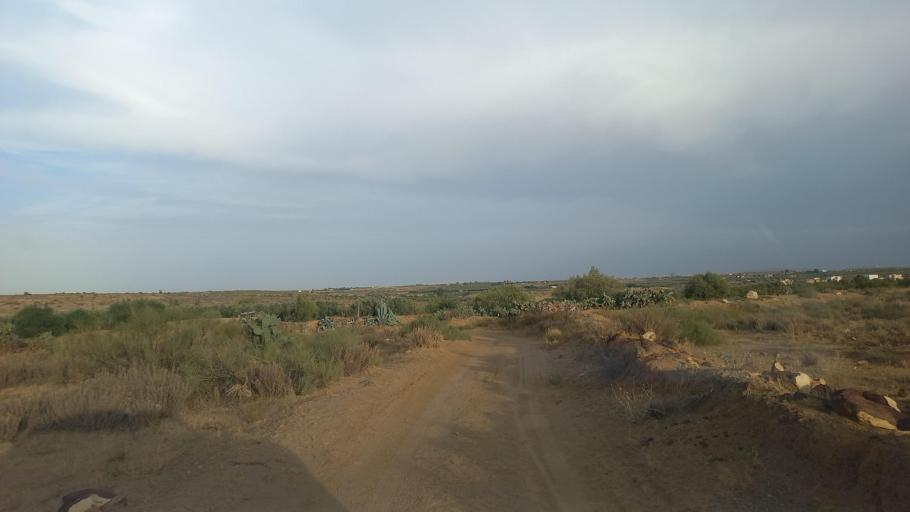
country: TN
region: Al Qasrayn
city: Kasserine
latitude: 35.2151
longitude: 9.0594
